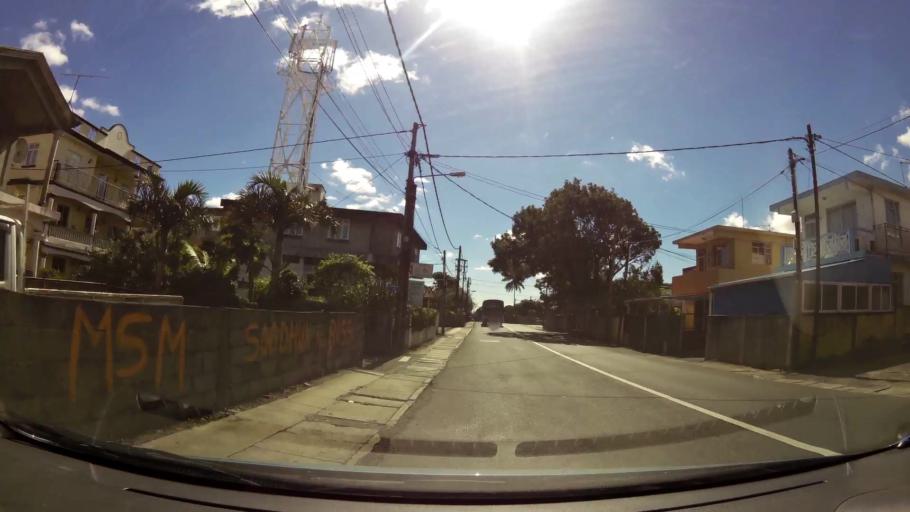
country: MU
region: Plaines Wilhems
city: Vacoas
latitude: -20.2883
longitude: 57.4813
